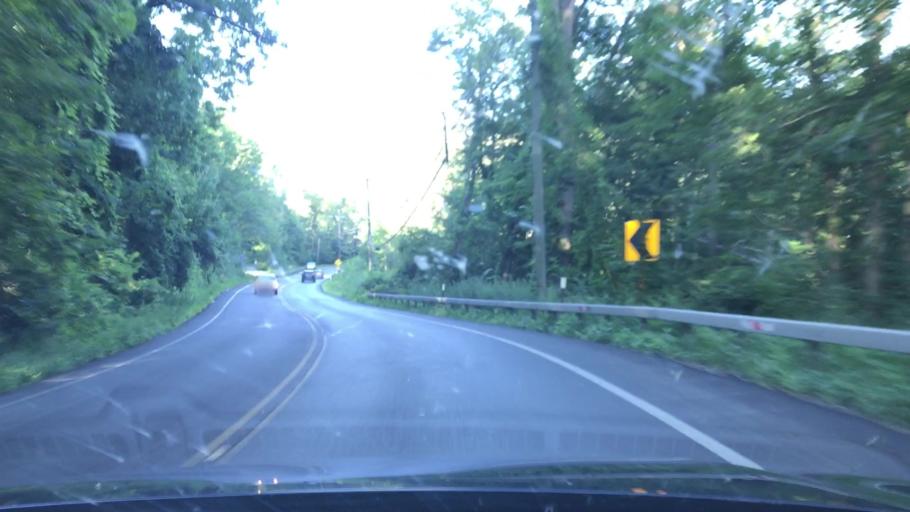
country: US
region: New York
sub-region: Putnam County
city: Mahopac
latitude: 41.3764
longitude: -73.7135
